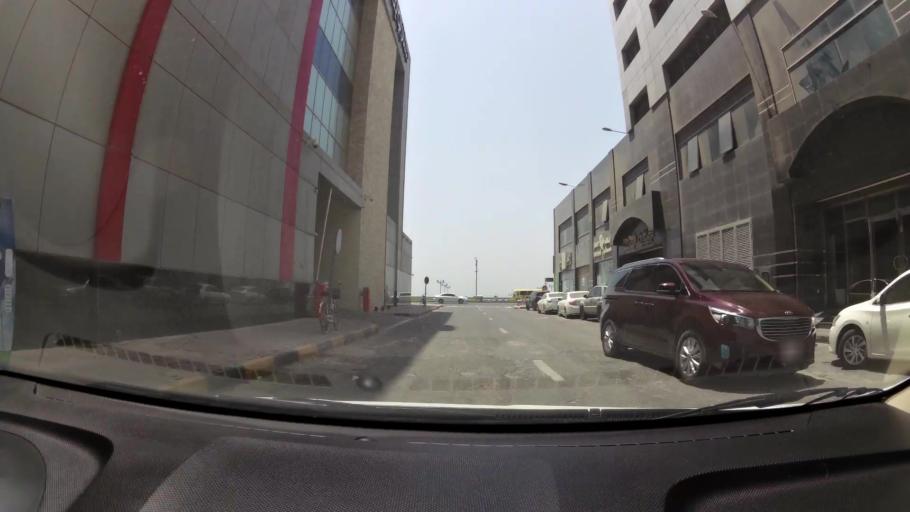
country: AE
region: Ajman
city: Ajman
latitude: 25.4034
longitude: 55.4296
